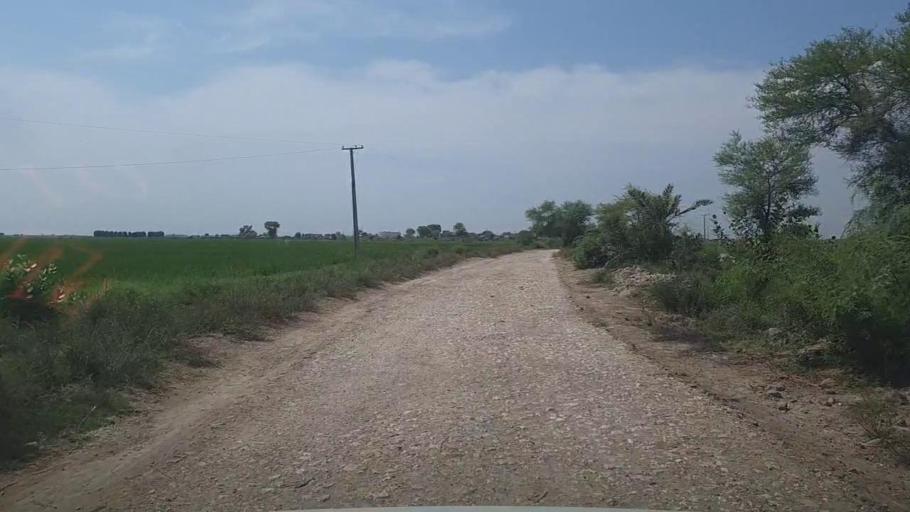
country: PK
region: Sindh
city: Kandhkot
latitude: 28.3104
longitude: 69.2318
